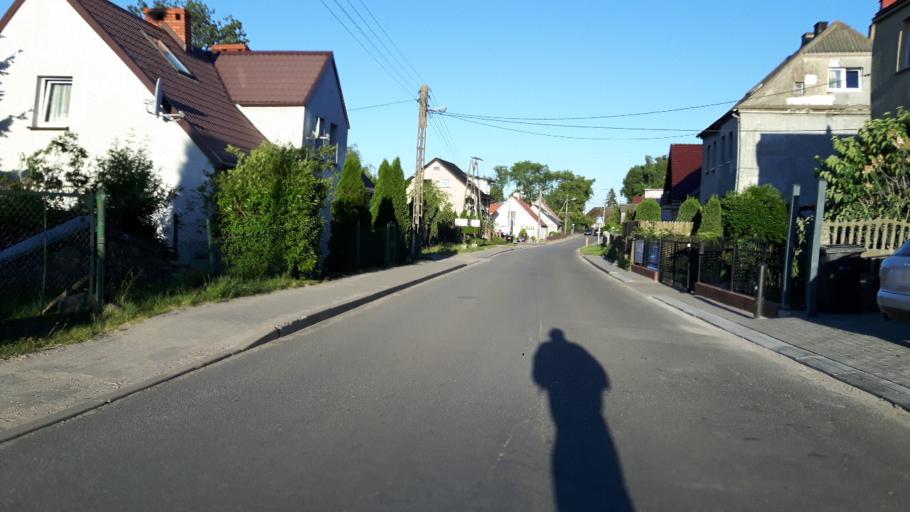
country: PL
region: Pomeranian Voivodeship
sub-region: Powiat pucki
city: Mosty
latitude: 54.6099
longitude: 18.5092
